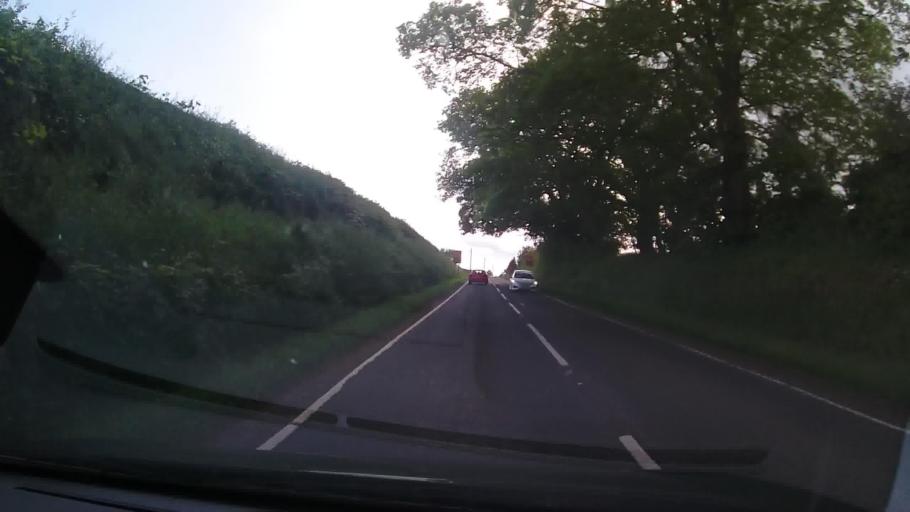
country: GB
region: England
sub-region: Shropshire
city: Clive
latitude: 52.8116
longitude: -2.7470
